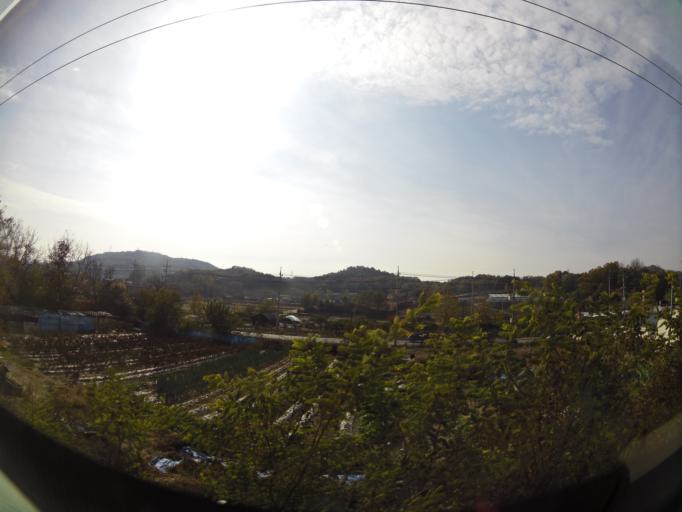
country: KR
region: Daejeon
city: Songgang-dong
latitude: 36.5377
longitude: 127.3436
